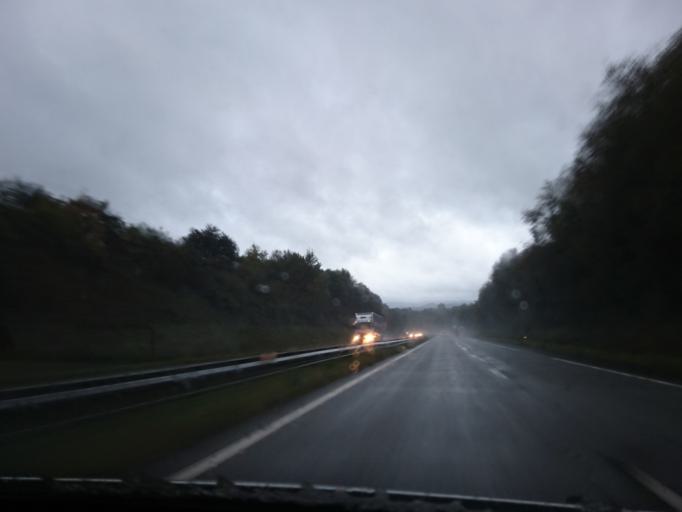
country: FR
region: Brittany
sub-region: Departement du Finistere
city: Le Faou
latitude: 48.2725
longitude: -4.1180
